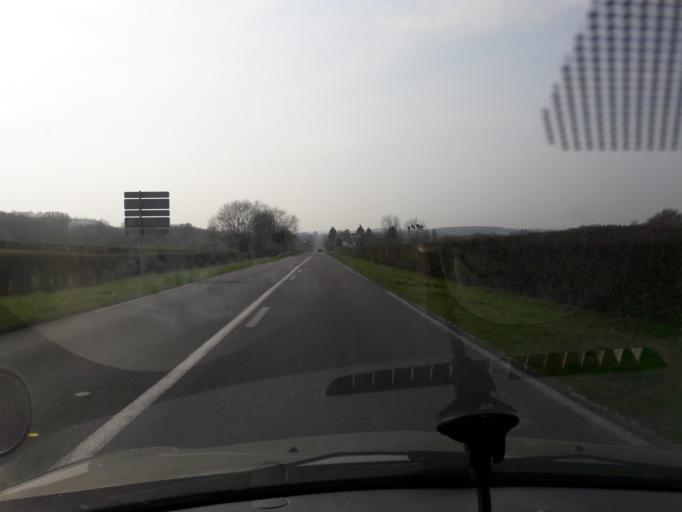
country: FR
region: Nord-Pas-de-Calais
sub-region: Departement du Nord
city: Jeumont
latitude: 50.2512
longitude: 4.0991
